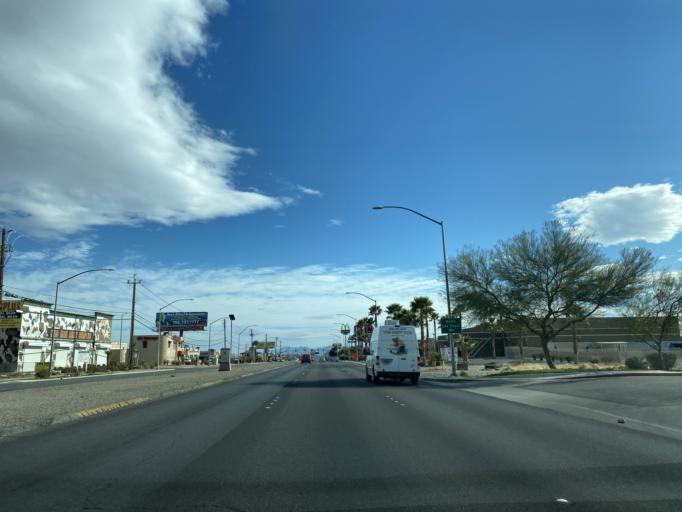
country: US
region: Nevada
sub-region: Clark County
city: Las Vegas
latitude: 36.2194
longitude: -115.2143
